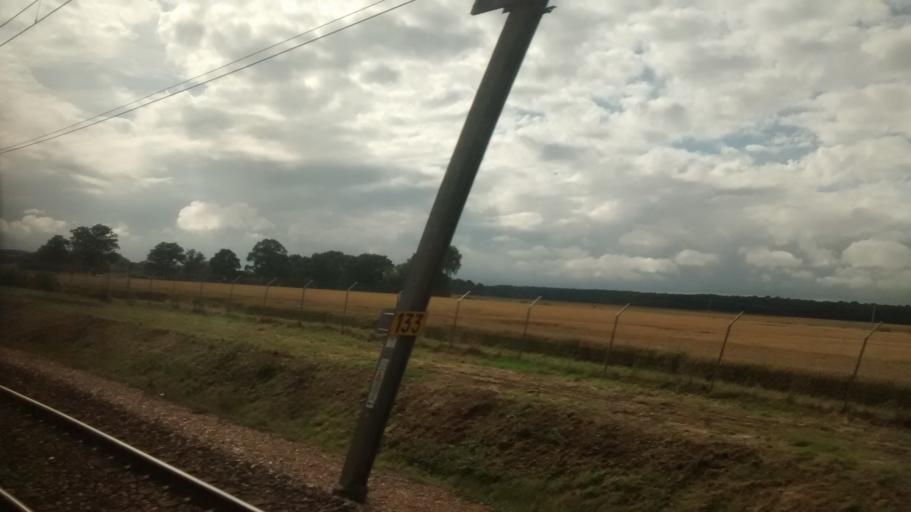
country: FR
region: Centre
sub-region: Departement du Loir-et-Cher
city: Droue
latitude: 48.0780
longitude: 1.0821
